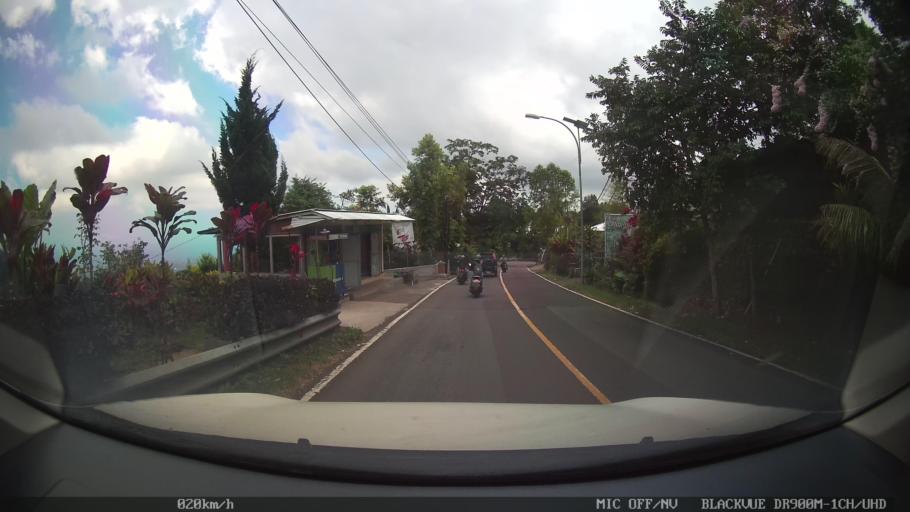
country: ID
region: Bali
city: Banjar Ambengan
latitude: -8.1974
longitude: 115.1394
